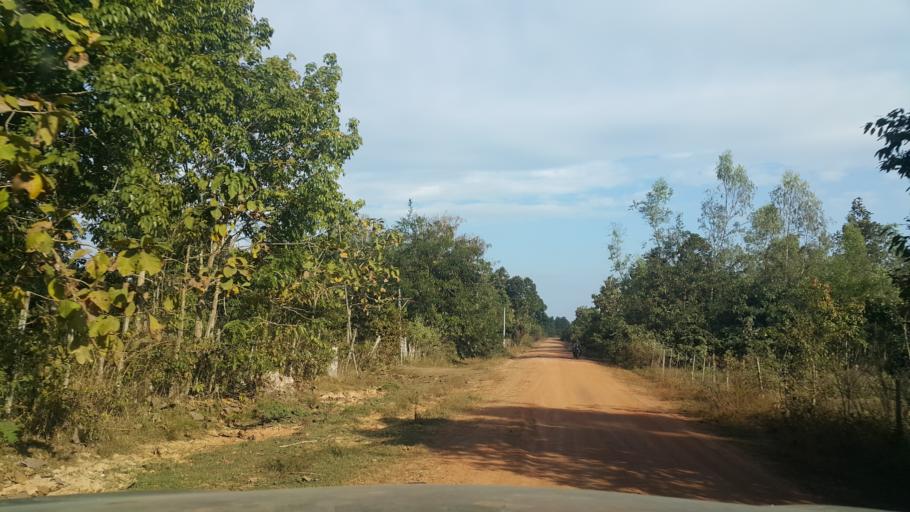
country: TH
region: Lampang
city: Hang Chat
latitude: 18.2923
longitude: 99.3565
